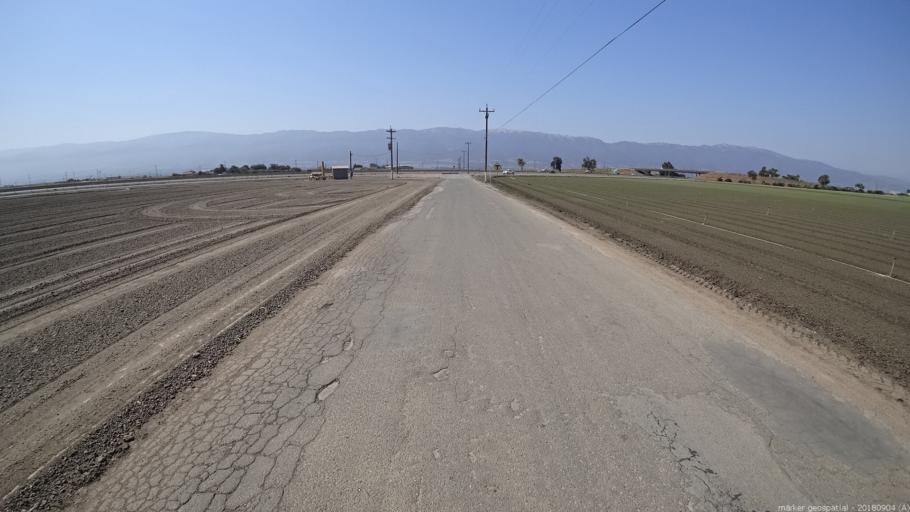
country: US
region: California
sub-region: Monterey County
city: Gonzales
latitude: 36.5240
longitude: -121.4599
